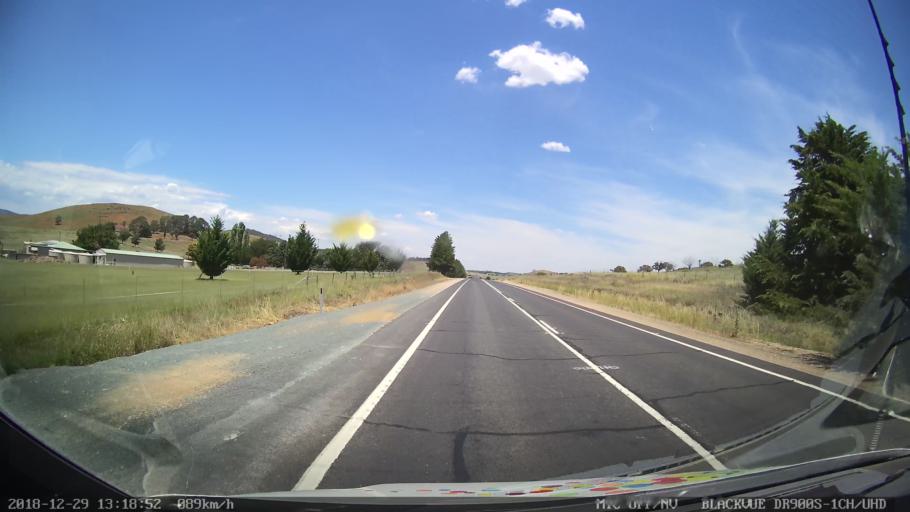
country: AU
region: Australian Capital Territory
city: Macarthur
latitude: -35.7572
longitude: 149.1611
